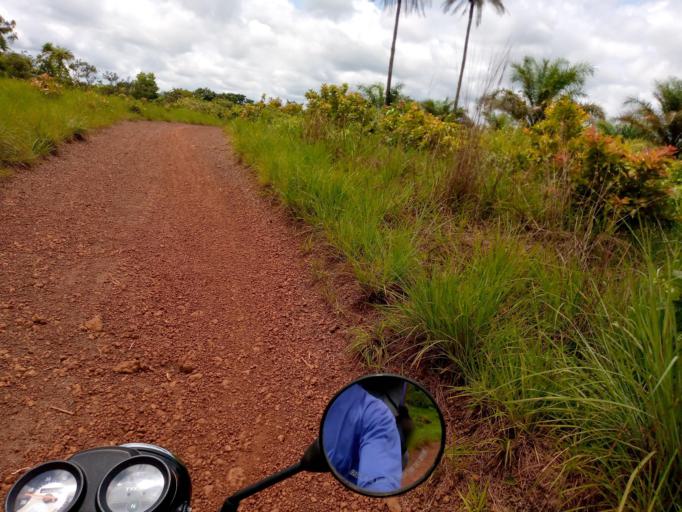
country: SL
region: Northern Province
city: Mange
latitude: 8.9905
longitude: -12.7863
